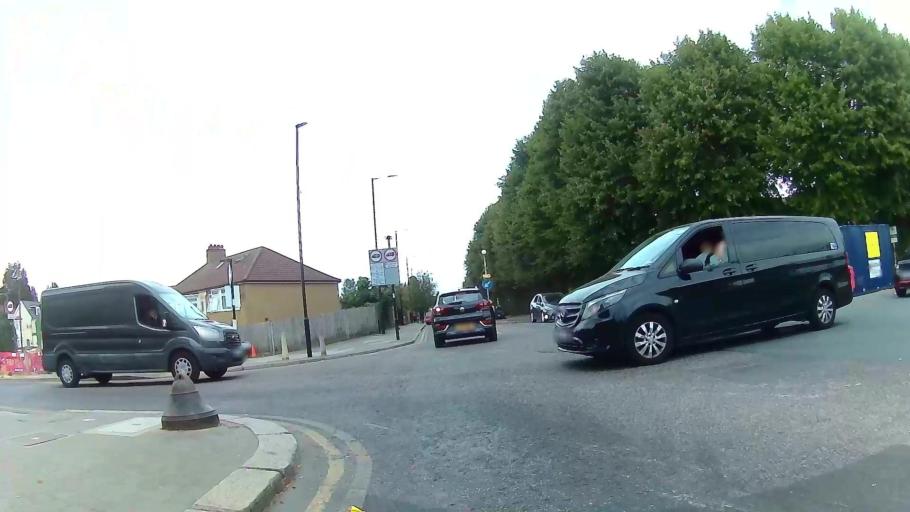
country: GB
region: England
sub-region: Greater London
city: Harringay
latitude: 51.6119
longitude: -0.0760
